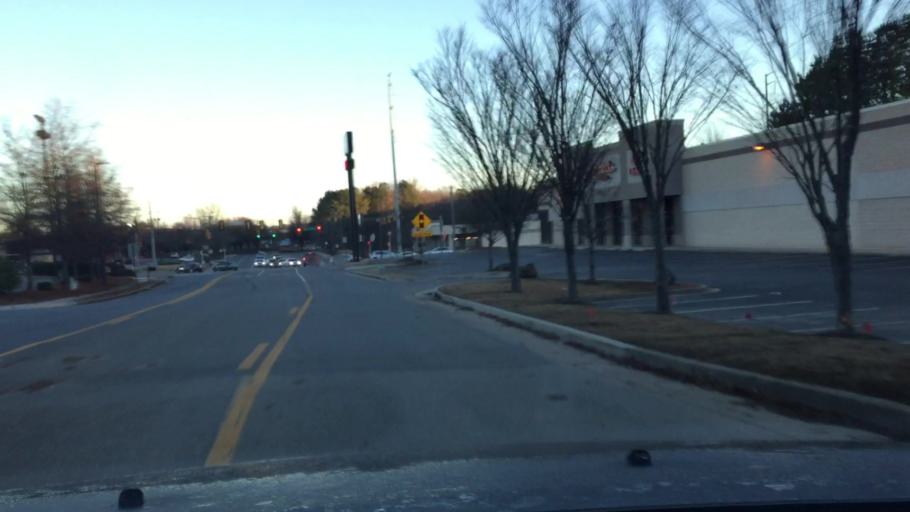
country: US
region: Georgia
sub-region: Cobb County
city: Marietta
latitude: 34.0127
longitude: -84.5546
